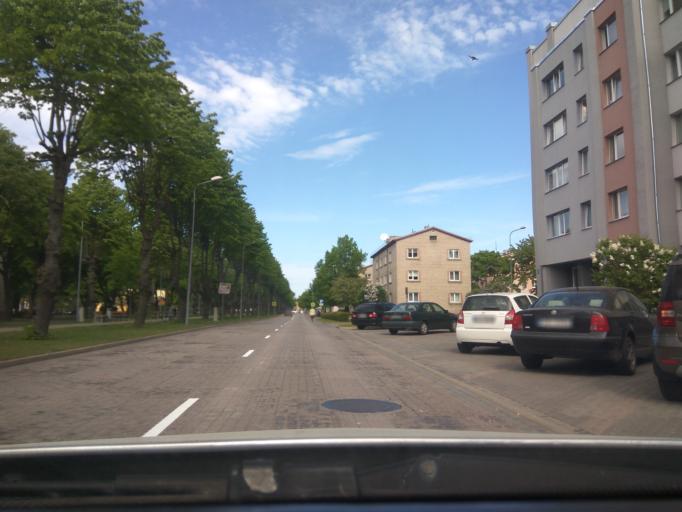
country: LV
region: Ventspils
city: Ventspils
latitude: 57.3913
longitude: 21.5782
